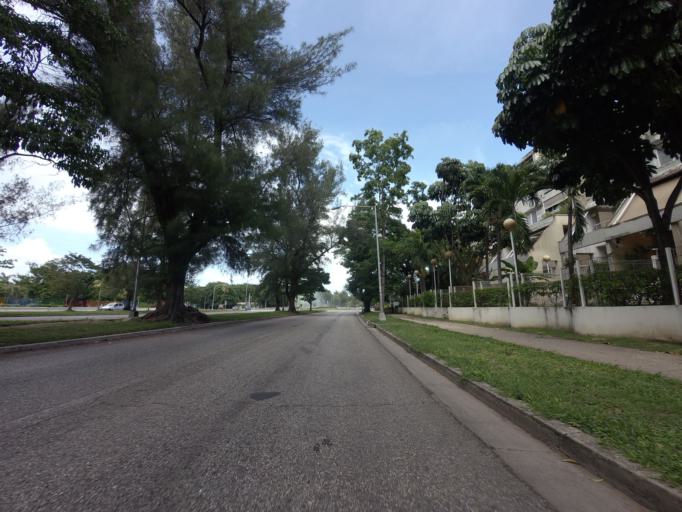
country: CU
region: La Habana
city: Cerro
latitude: 23.0970
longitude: -82.4510
